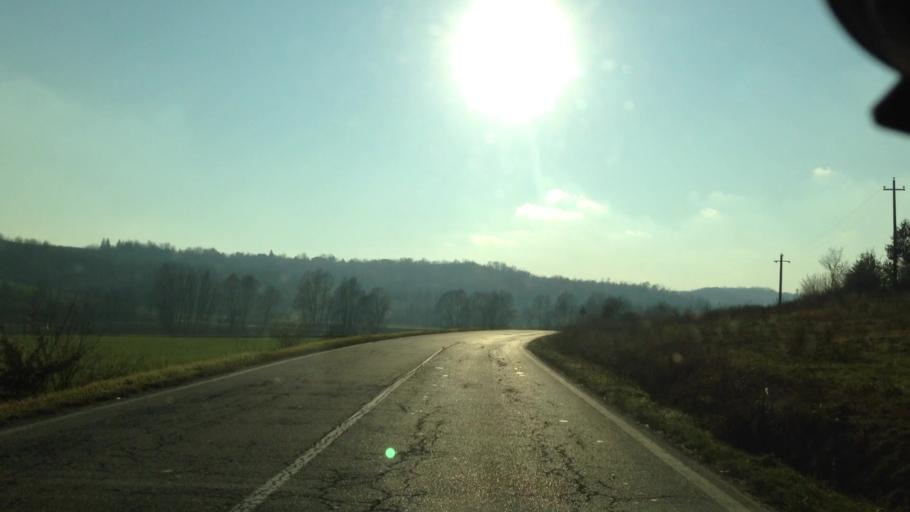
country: IT
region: Piedmont
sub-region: Provincia di Alessandria
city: Masio
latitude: 44.8418
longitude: 8.3911
